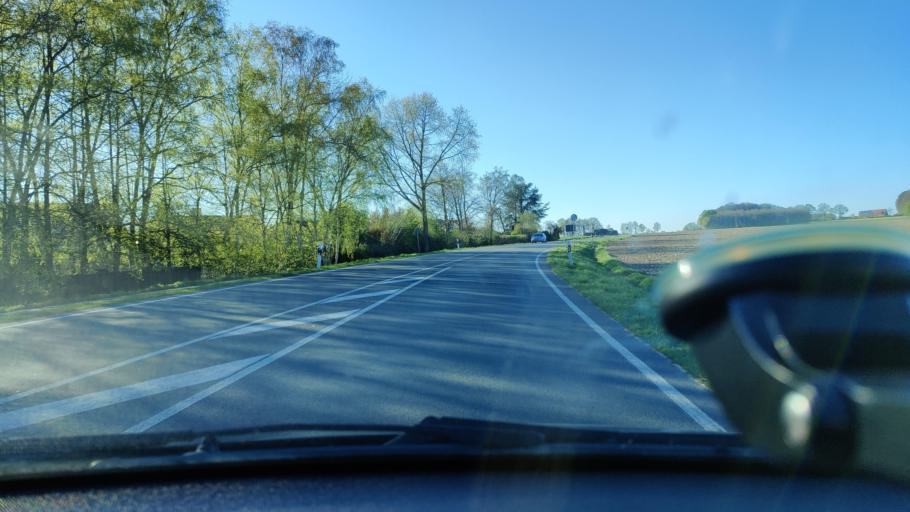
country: DE
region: North Rhine-Westphalia
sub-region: Regierungsbezirk Munster
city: Coesfeld
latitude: 51.9811
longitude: 7.1451
